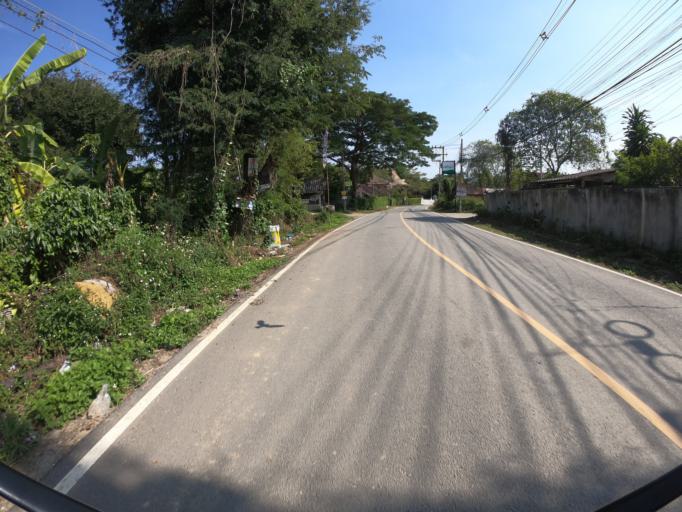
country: TH
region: Chiang Mai
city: San Sai
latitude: 18.8463
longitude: 99.0011
